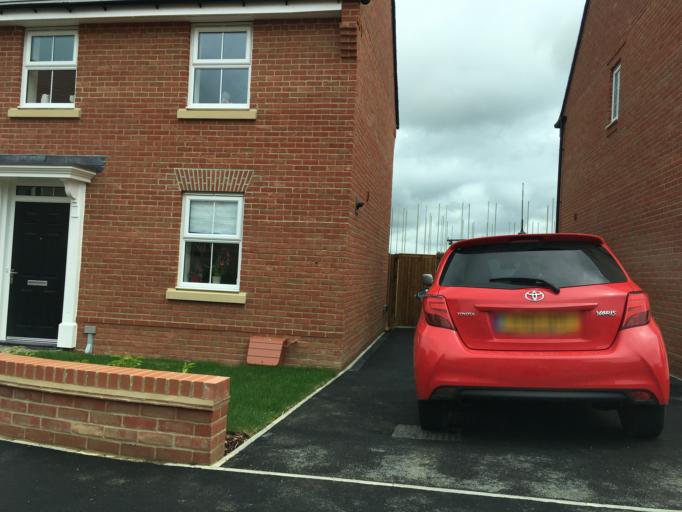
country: GB
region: England
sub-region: Milton Keynes
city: Woburn Sands
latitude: 52.0328
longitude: -0.6555
